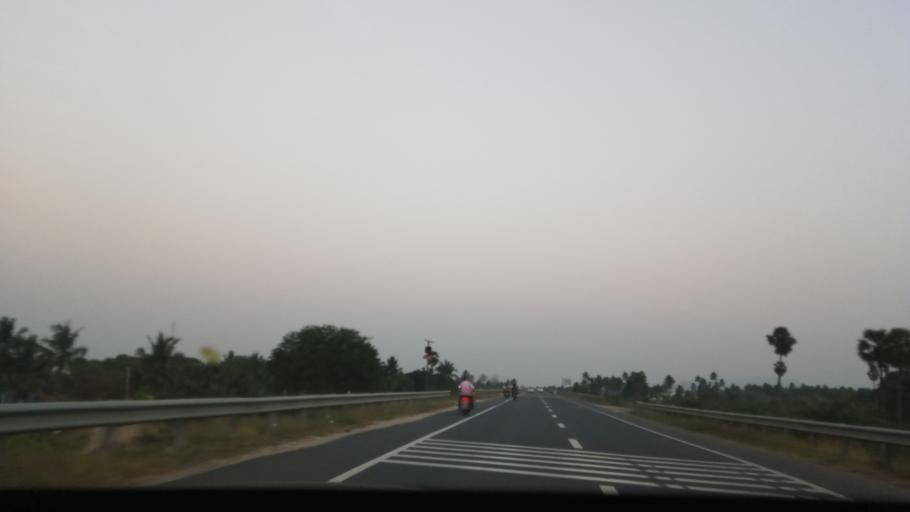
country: IN
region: Tamil Nadu
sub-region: Salem
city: Belur
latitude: 11.6522
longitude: 78.3873
